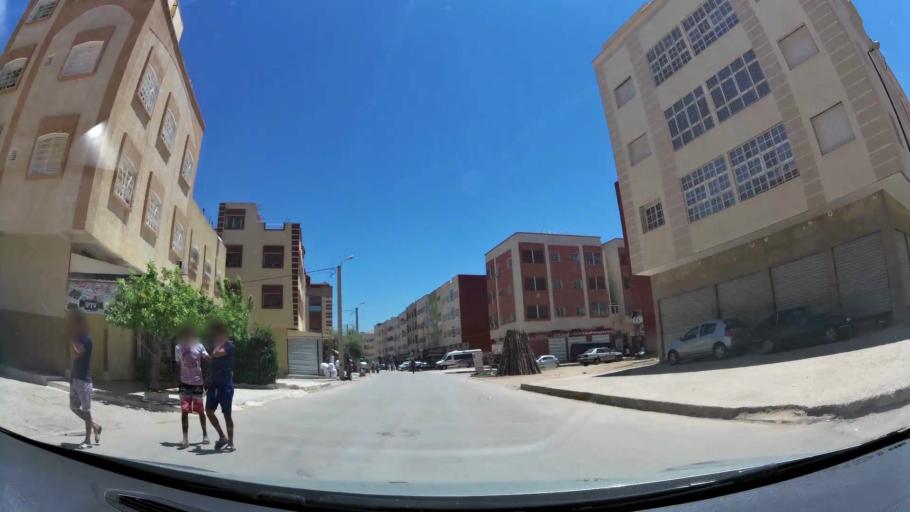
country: MA
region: Meknes-Tafilalet
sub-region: Meknes
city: Meknes
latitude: 33.8618
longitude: -5.5652
